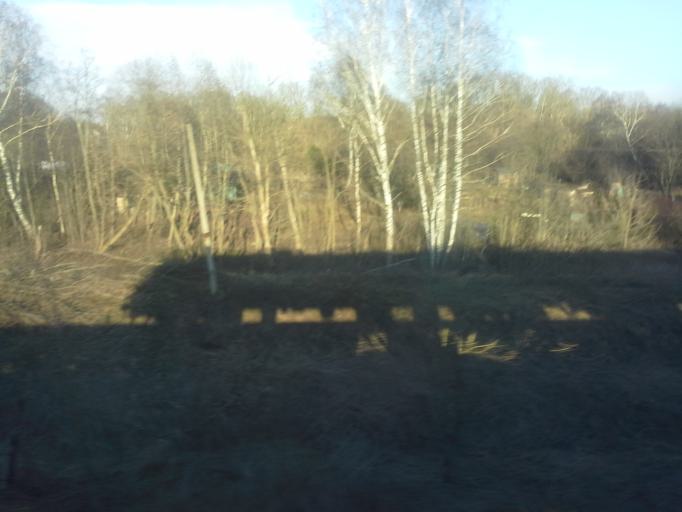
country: RU
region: Moskovskaya
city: Podosinki
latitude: 56.2008
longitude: 37.5251
